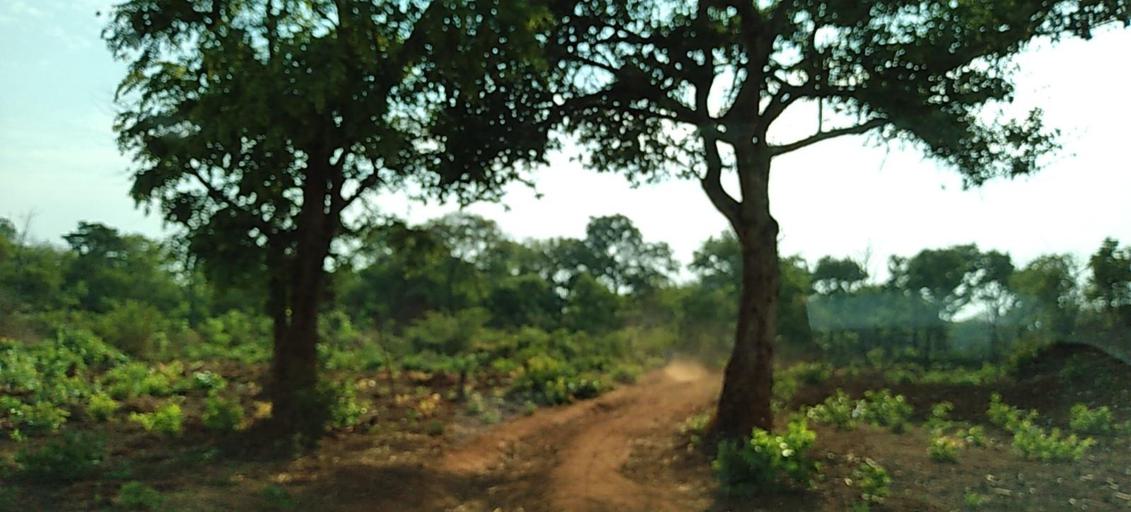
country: ZM
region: Copperbelt
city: Kalulushi
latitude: -12.9638
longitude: 27.7051
